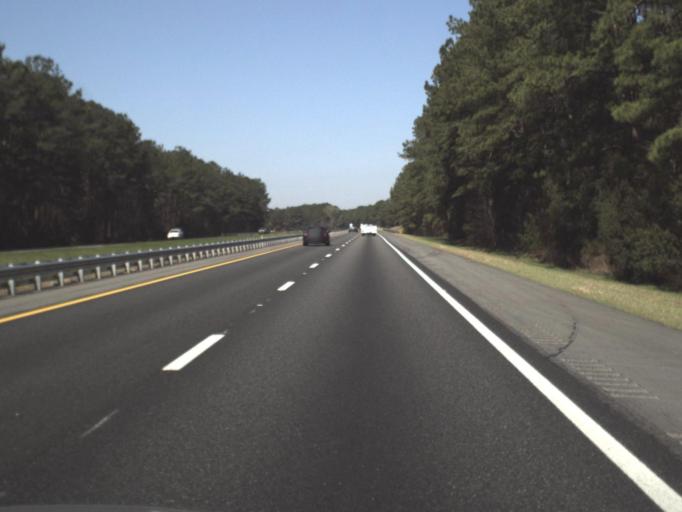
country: US
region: Florida
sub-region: Gadsden County
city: Gretna
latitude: 30.6173
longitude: -84.7675
